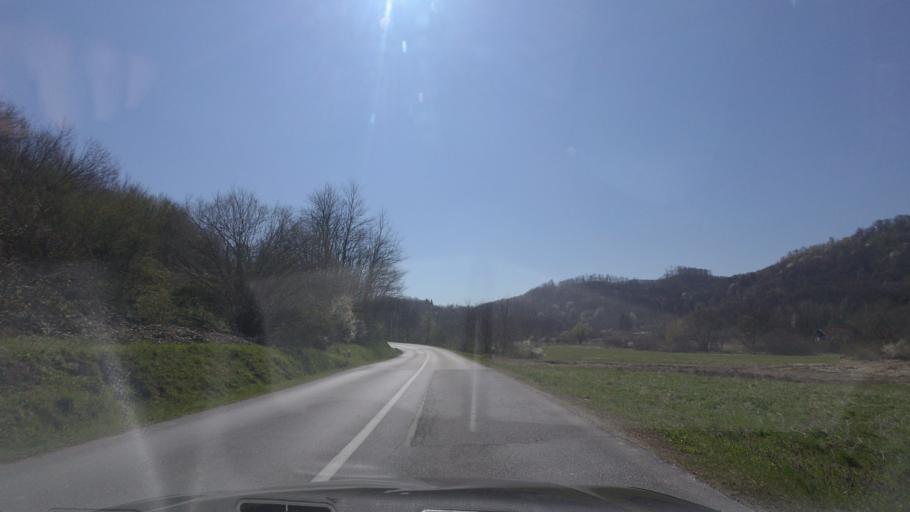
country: HR
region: Karlovacka
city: Vojnic
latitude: 45.3511
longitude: 15.6766
